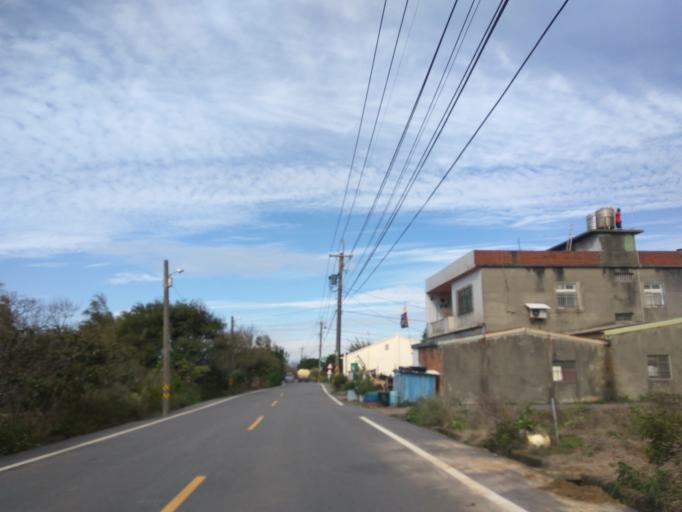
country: TW
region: Taiwan
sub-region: Hsinchu
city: Zhubei
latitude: 24.9977
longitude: 121.0902
